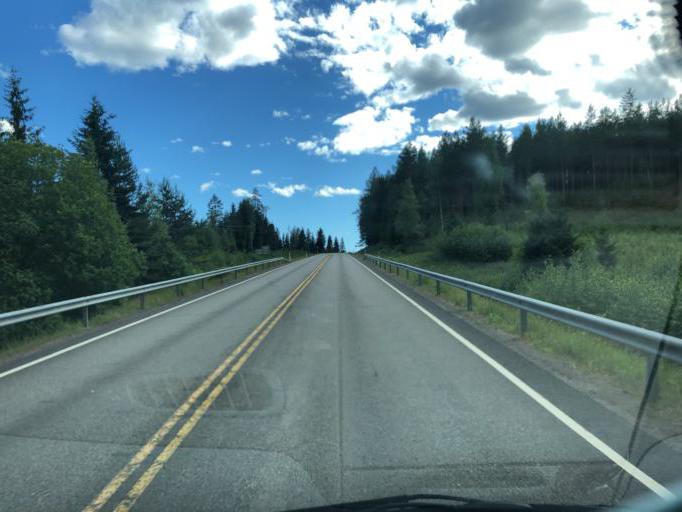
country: FI
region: Kymenlaakso
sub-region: Kouvola
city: Kouvola
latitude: 60.9780
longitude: 26.9065
